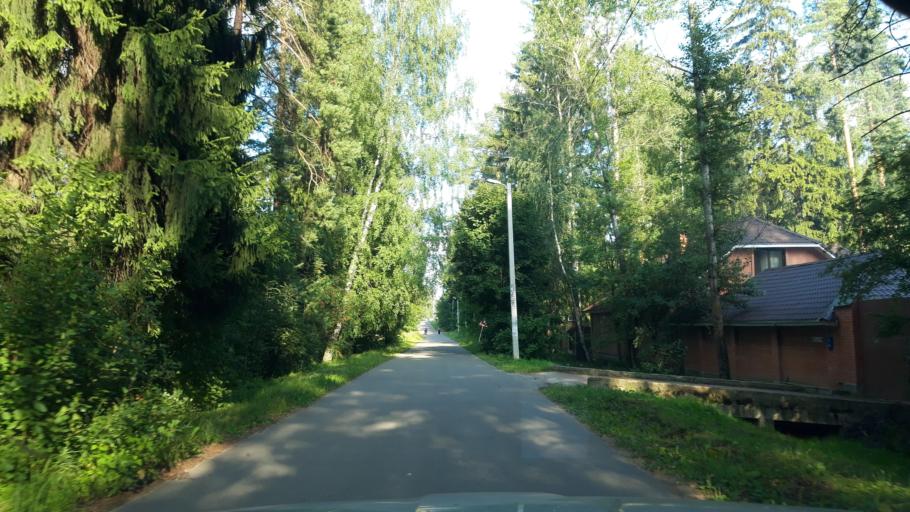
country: RU
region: Moskovskaya
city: Povarovo
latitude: 56.0625
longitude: 37.0804
